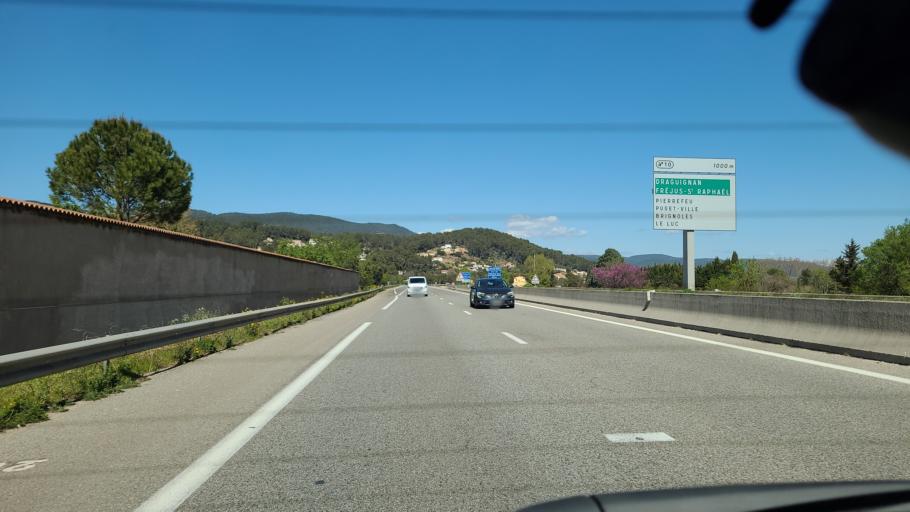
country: FR
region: Provence-Alpes-Cote d'Azur
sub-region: Departement du Var
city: Cuers
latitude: 43.2379
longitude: 6.0842
